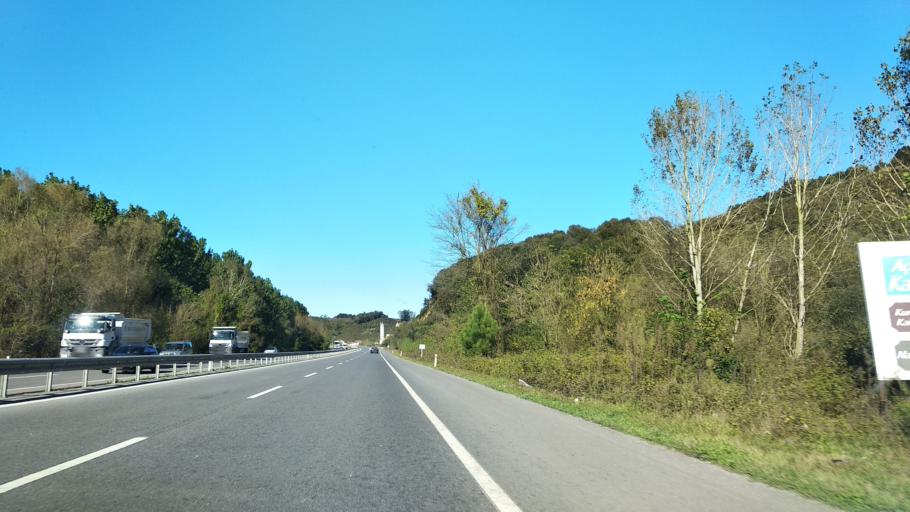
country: TR
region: Sakarya
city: Karasu
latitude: 41.0700
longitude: 30.6450
